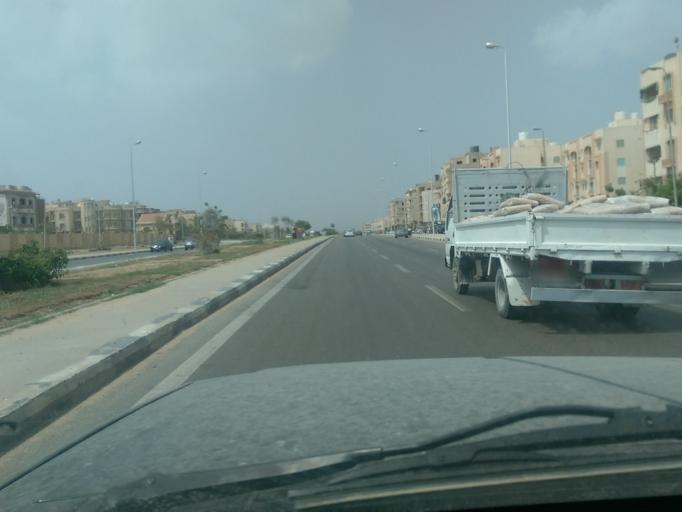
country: EG
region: Muhafazat al Qahirah
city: Cairo
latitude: 29.9965
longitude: 31.4409
